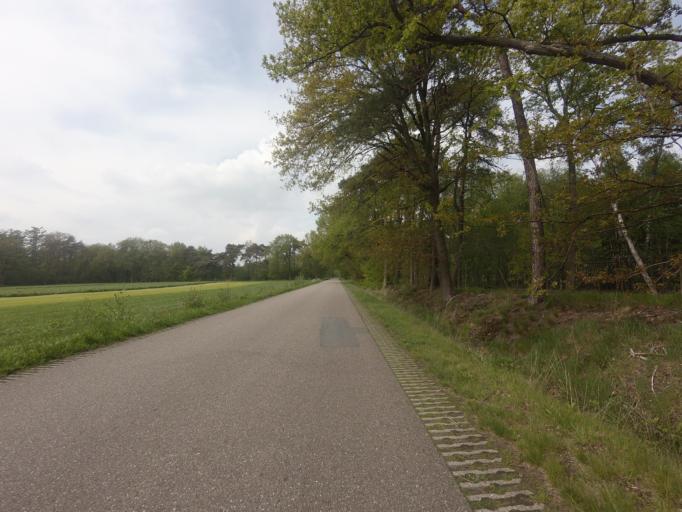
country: NL
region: Overijssel
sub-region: Gemeente Hof van Twente
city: Delden
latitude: 52.2552
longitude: 6.6770
